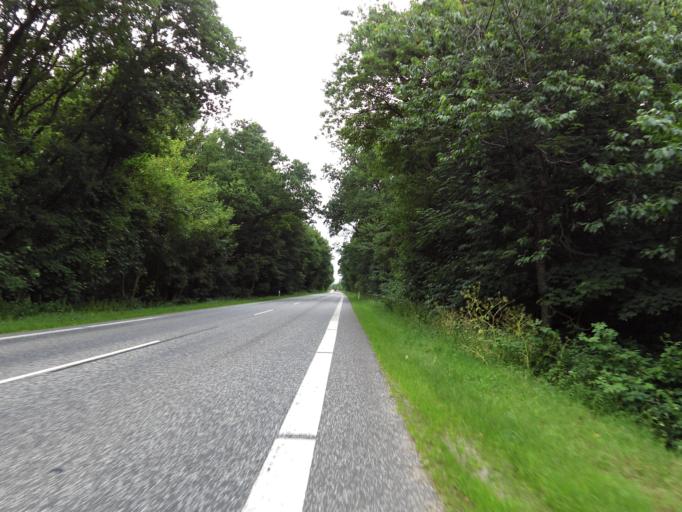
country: DK
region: South Denmark
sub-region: Tonder Kommune
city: Logumkloster
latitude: 55.0954
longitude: 8.9384
